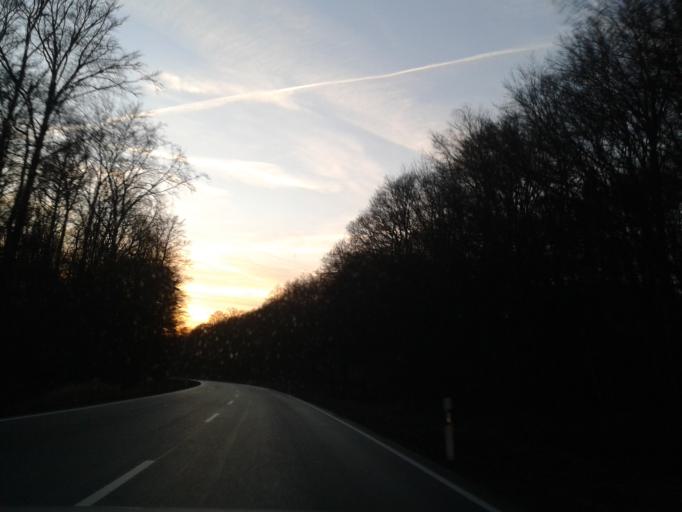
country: DE
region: Bavaria
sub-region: Regierungsbezirk Unterfranken
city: Aidhausen
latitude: 50.1114
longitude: 10.4236
